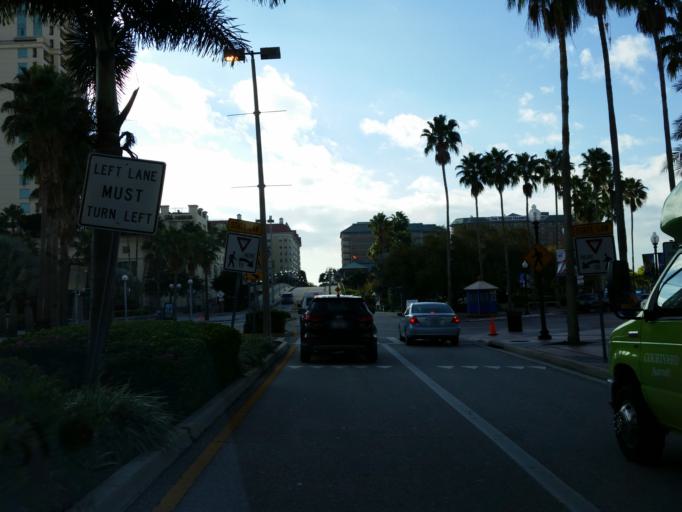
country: US
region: Florida
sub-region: Hillsborough County
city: Tampa
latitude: 27.9418
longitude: -82.4554
